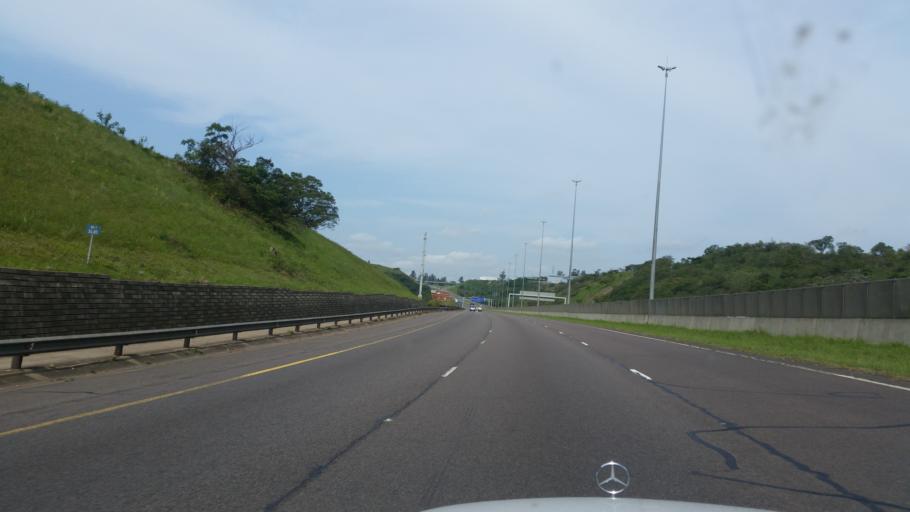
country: ZA
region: KwaZulu-Natal
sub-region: eThekwini Metropolitan Municipality
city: Berea
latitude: -29.8263
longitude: 30.8159
